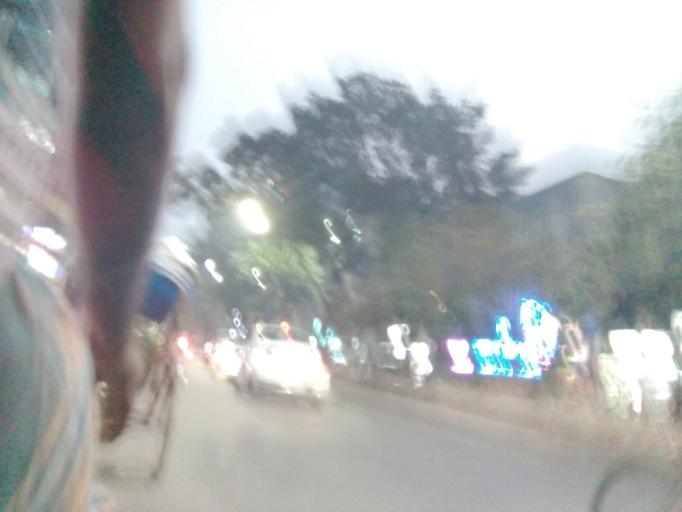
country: BD
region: Dhaka
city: Paltan
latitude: 23.7335
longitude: 90.4101
